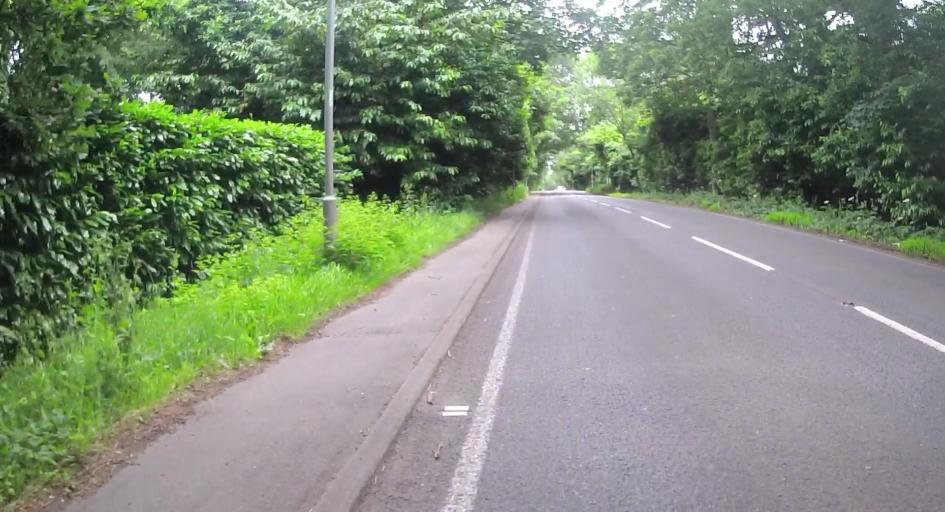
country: GB
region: England
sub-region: Wokingham
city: Winnersh
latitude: 51.4168
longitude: -0.8809
